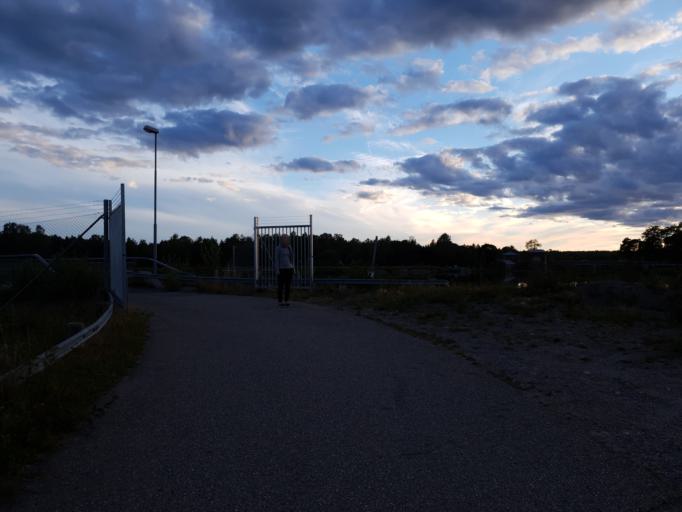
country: SE
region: Gaevleborg
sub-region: Soderhamns Kommun
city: Ljusne
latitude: 61.2075
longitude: 17.1212
